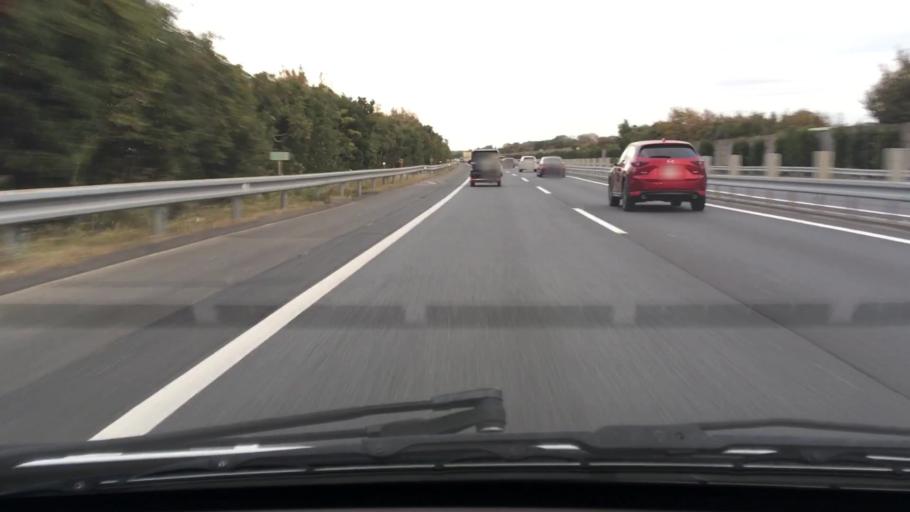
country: JP
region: Chiba
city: Ichihara
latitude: 35.5135
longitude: 140.1155
